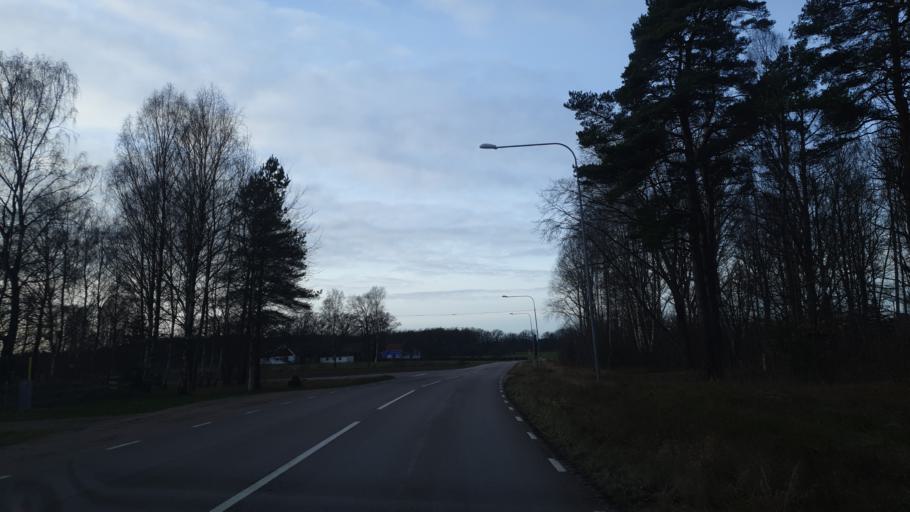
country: SE
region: Kalmar
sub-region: Torsas Kommun
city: Torsas
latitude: 56.2548
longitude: 16.0118
